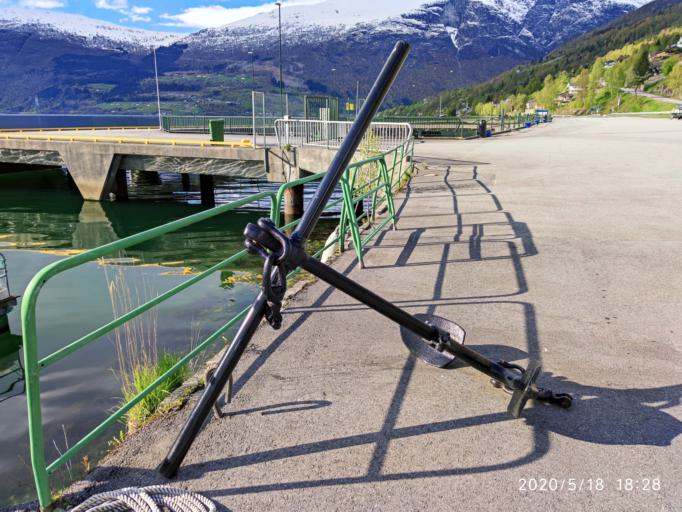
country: NO
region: Sogn og Fjordane
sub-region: Stryn
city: Stryn
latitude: 61.8426
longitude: 6.8105
